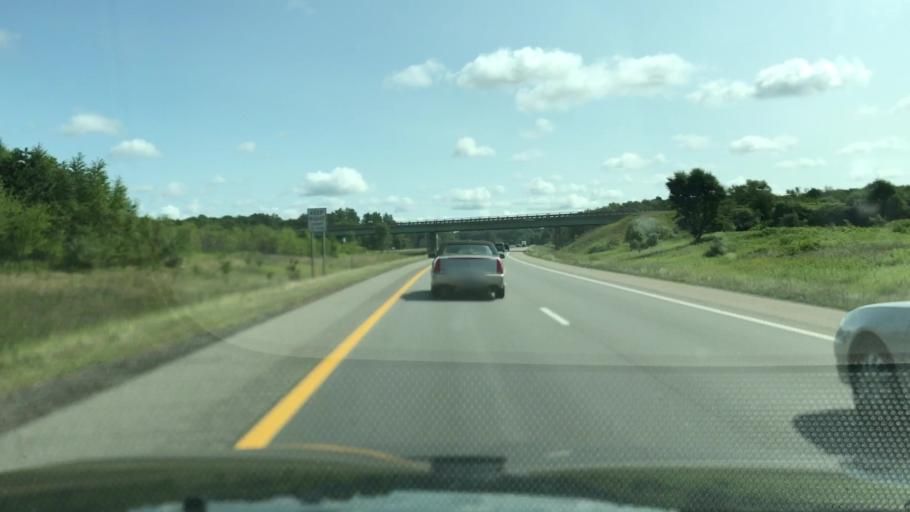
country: US
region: Michigan
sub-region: Kent County
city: Cedar Springs
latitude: 43.3086
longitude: -85.5342
